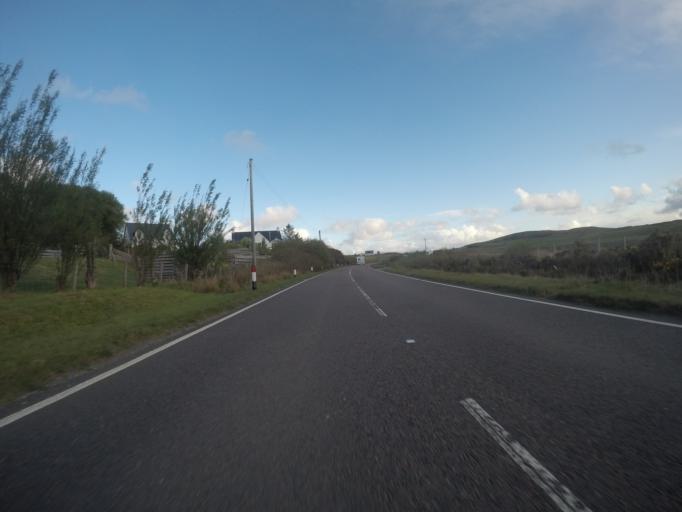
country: GB
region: Scotland
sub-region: Highland
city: Portree
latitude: 57.4804
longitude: -6.3009
